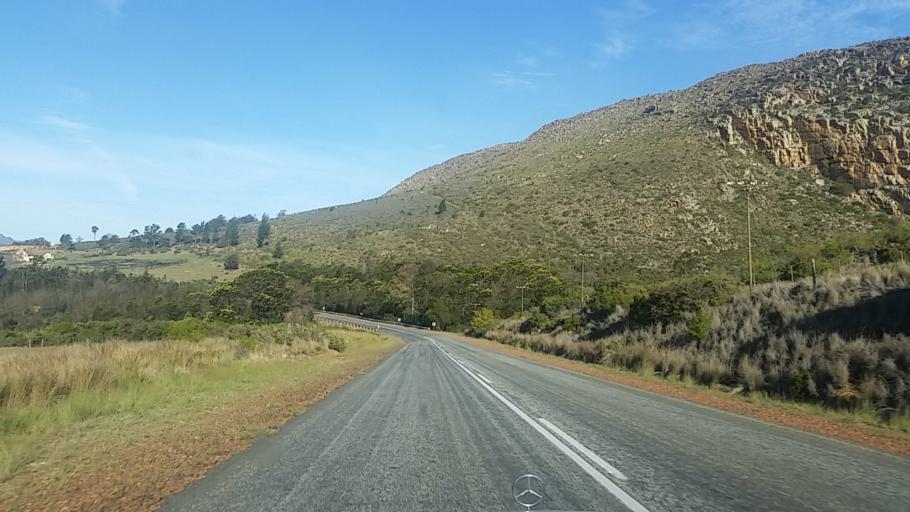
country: ZA
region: Western Cape
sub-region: Eden District Municipality
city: Knysna
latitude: -33.7739
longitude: 22.9544
